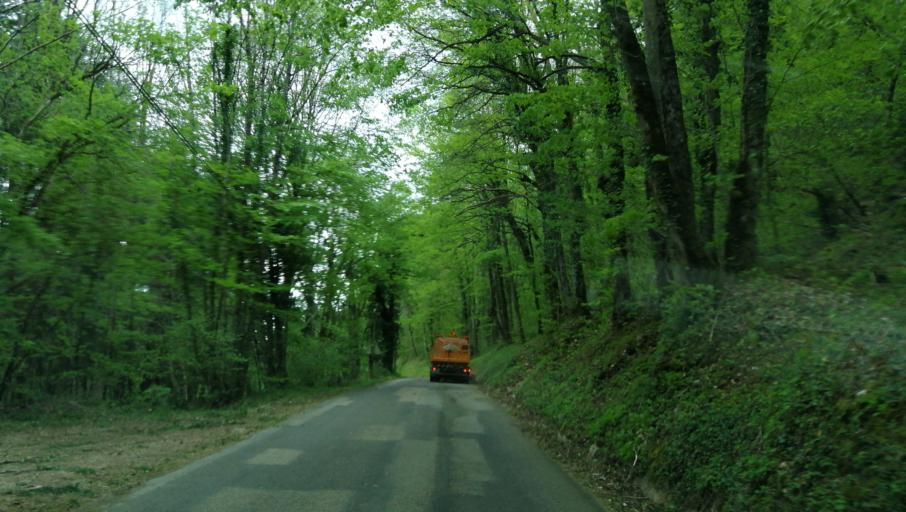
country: FR
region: Rhone-Alpes
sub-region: Departement de la Savoie
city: Brison-Saint-Innocent
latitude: 45.7164
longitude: 5.8516
